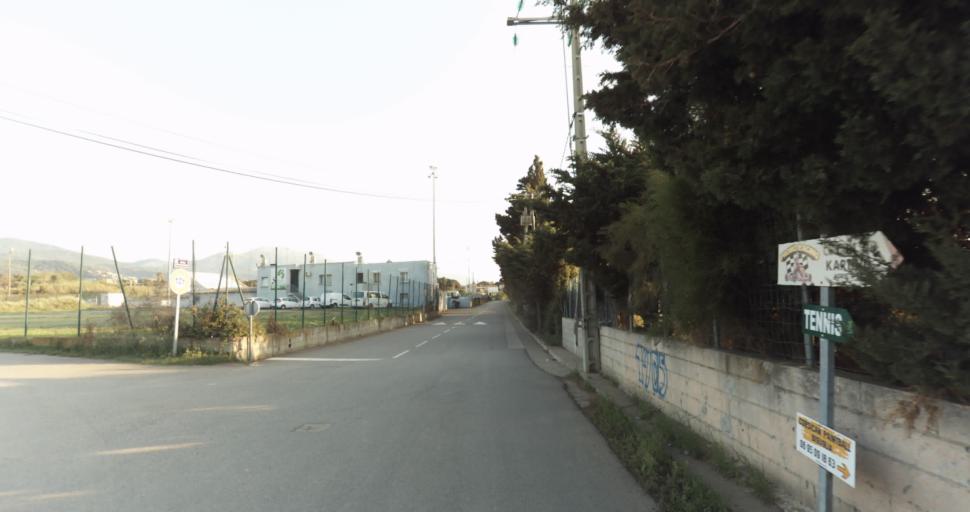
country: FR
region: Corsica
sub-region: Departement de la Haute-Corse
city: Biguglia
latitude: 42.6193
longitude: 9.4433
